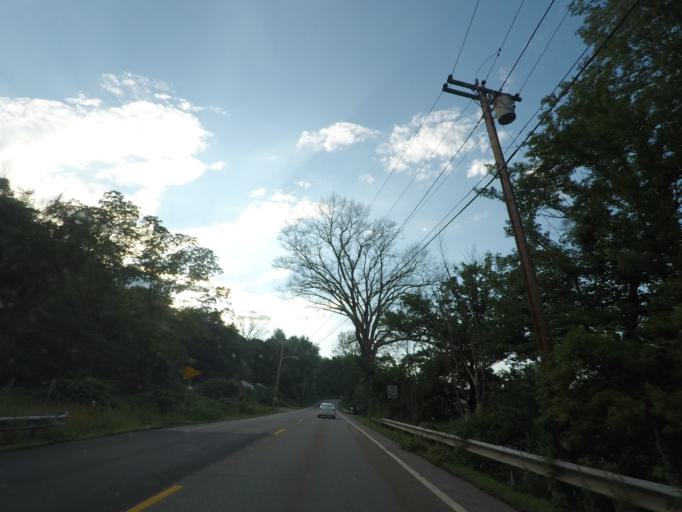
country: US
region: Massachusetts
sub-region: Worcester County
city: Southbridge
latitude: 42.0527
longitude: -71.9897
